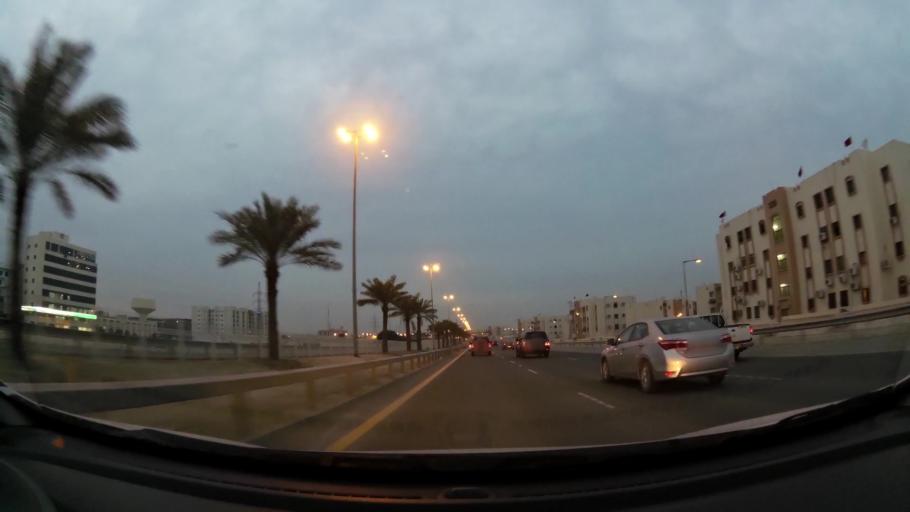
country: BH
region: Northern
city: Madinat `Isa
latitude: 26.1555
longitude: 50.5695
